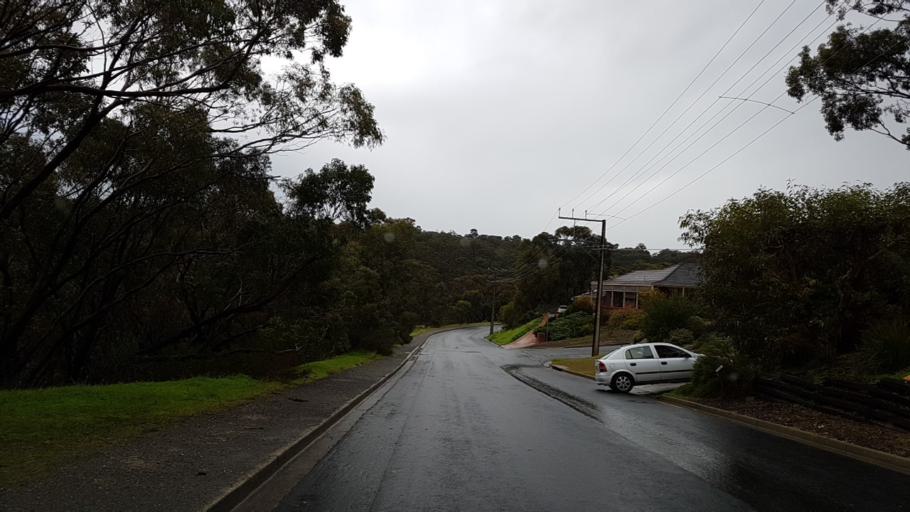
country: AU
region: South Australia
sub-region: Onkaparinga
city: Bedford Park
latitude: -35.0403
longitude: 138.5826
